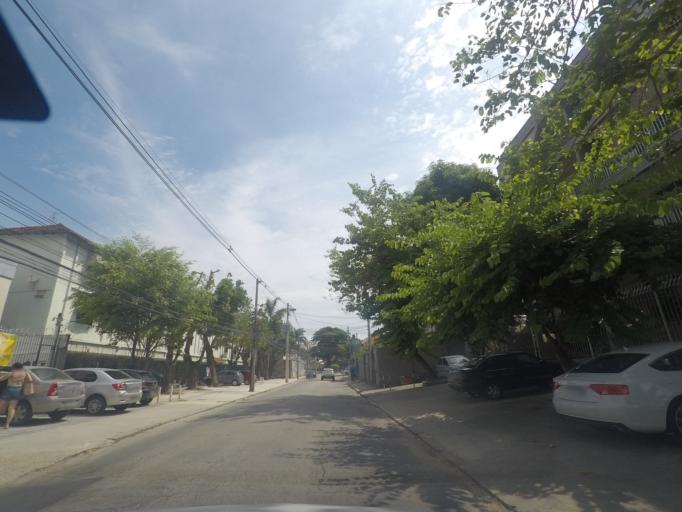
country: BR
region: Rio de Janeiro
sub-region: Rio De Janeiro
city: Rio de Janeiro
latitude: -22.8180
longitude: -43.1880
